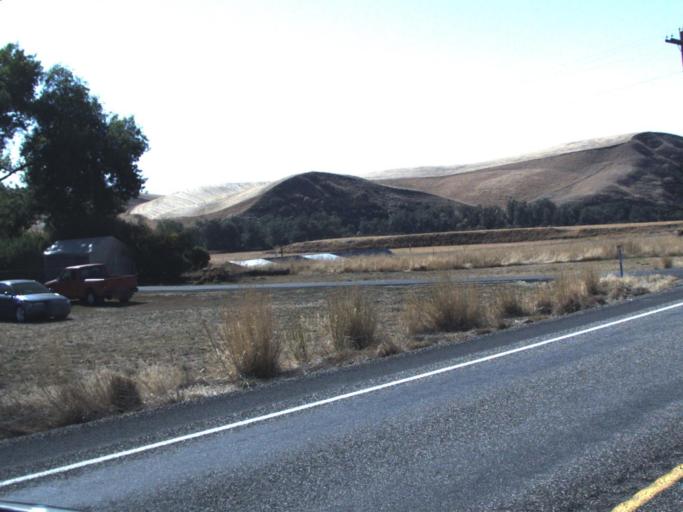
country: US
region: Washington
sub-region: Walla Walla County
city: Waitsburg
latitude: 46.2987
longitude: -118.3383
